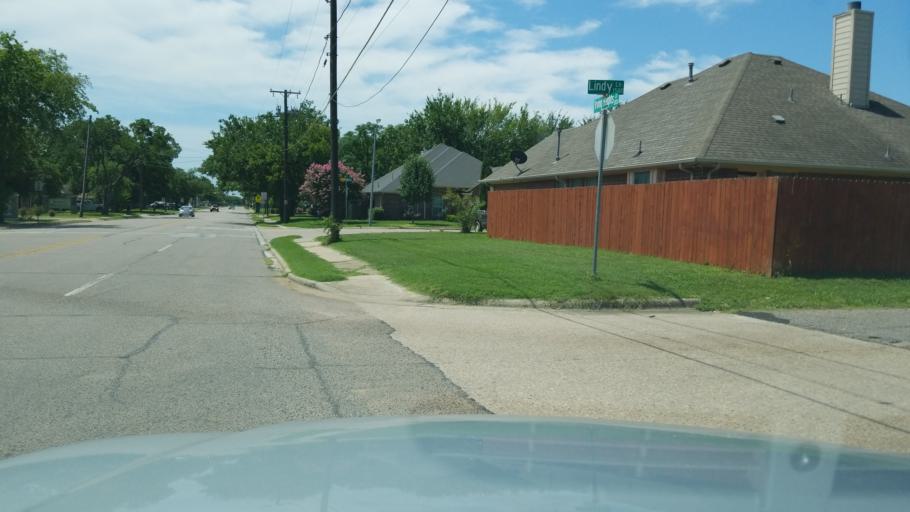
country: US
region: Texas
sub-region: Dallas County
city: Irving
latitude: 32.8036
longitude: -96.9257
